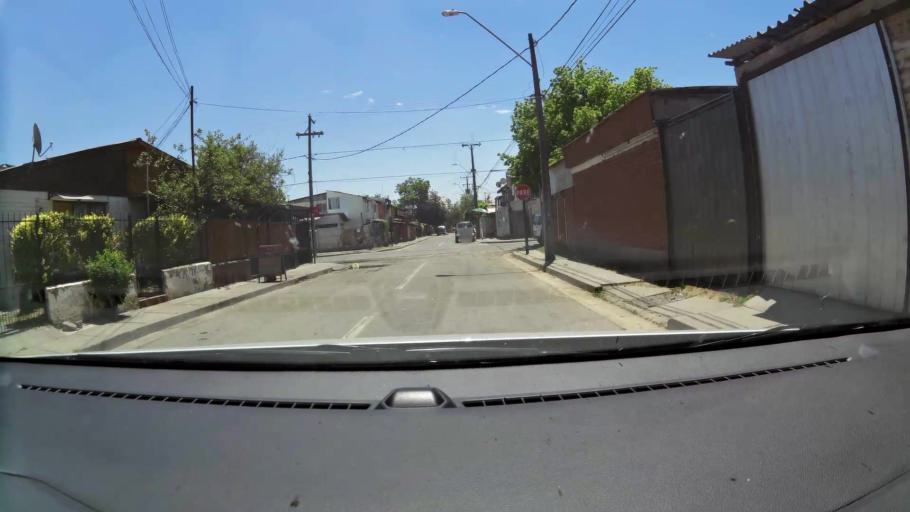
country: CL
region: Santiago Metropolitan
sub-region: Provincia de Santiago
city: La Pintana
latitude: -33.5588
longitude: -70.6543
